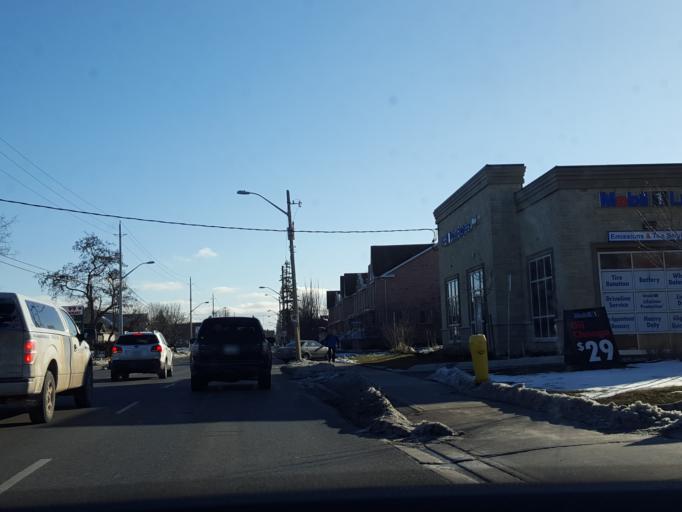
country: CA
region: Ontario
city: Ajax
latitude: 43.8860
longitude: -78.9448
